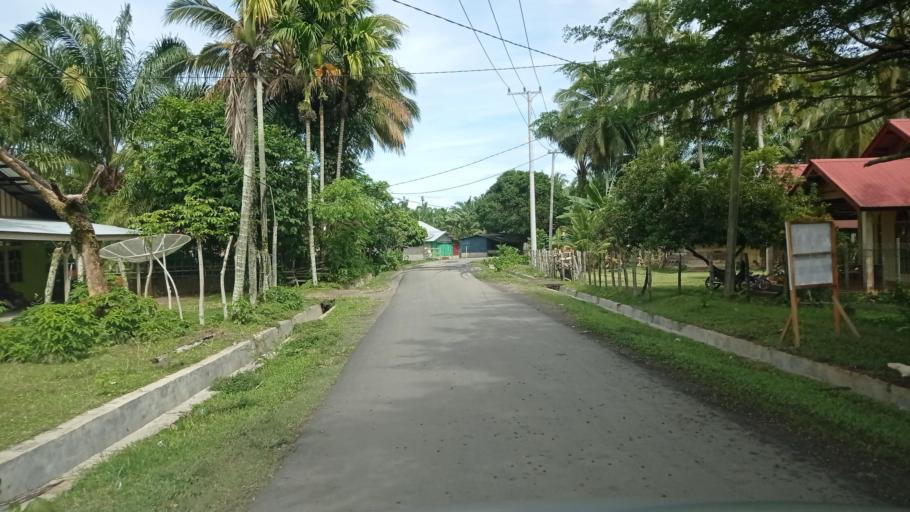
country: ID
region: Bengkulu
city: Ipuh
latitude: -2.5882
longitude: 101.1174
